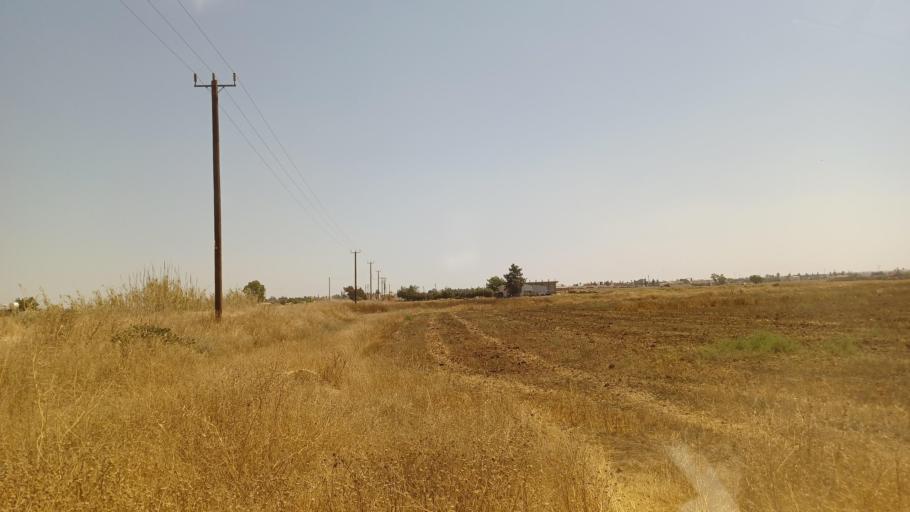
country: CY
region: Ammochostos
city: Avgorou
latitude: 35.0255
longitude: 33.8231
